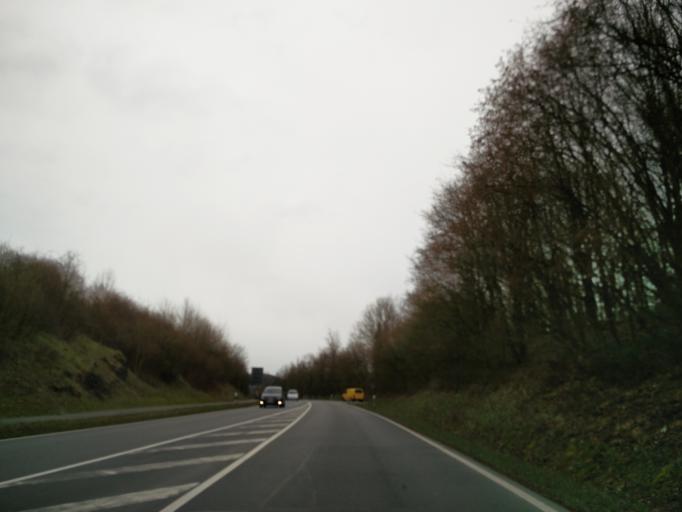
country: DE
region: North Rhine-Westphalia
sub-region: Regierungsbezirk Detmold
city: Horn
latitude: 51.8603
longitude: 8.9539
